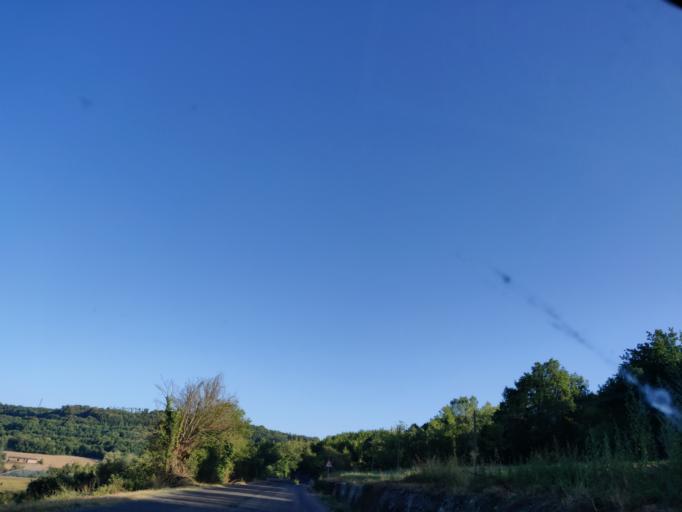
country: IT
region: Latium
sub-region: Provincia di Viterbo
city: Acquapendente
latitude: 42.7600
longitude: 11.8637
